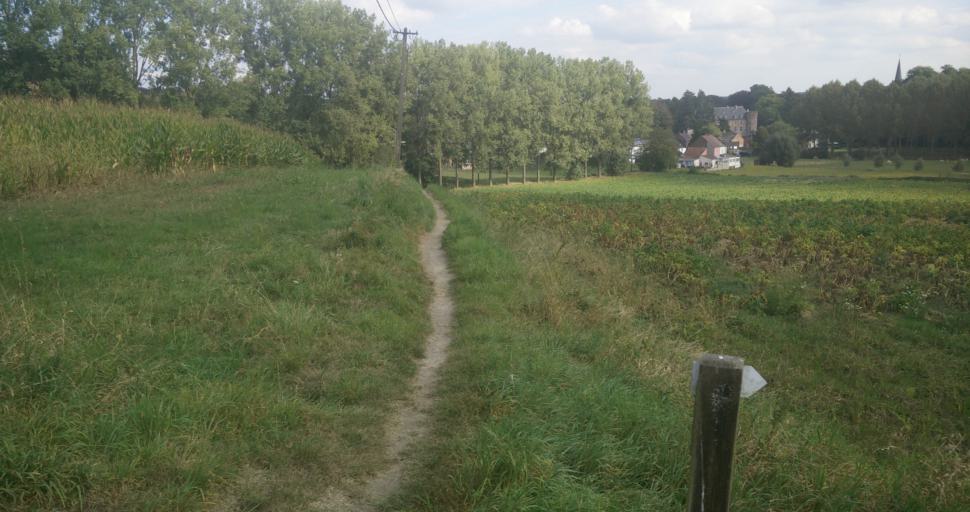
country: BE
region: Wallonia
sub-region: Province du Brabant Wallon
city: Braine-le-Chateau
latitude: 50.6842
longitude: 4.2591
